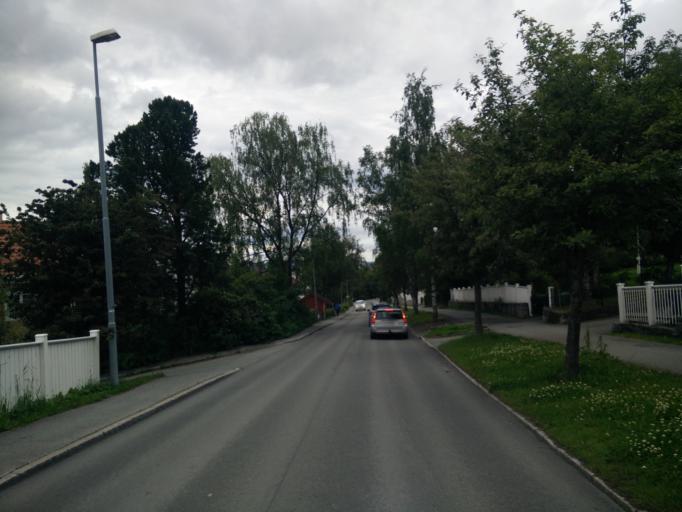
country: NO
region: Sor-Trondelag
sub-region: Trondheim
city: Trondheim
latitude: 63.4203
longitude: 10.4118
